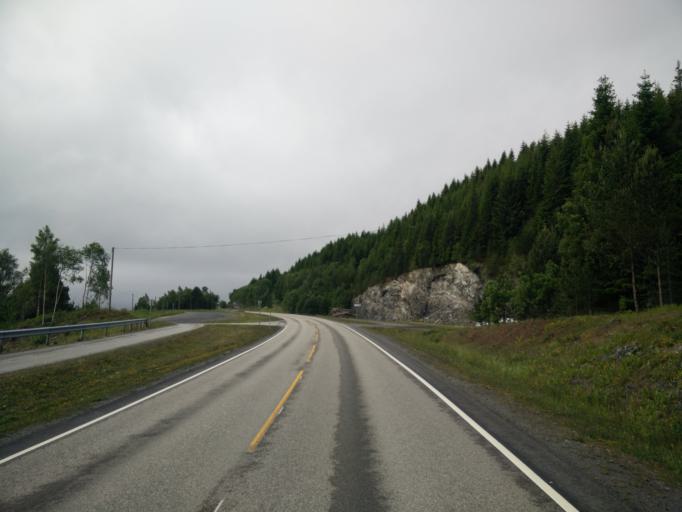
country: NO
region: More og Romsdal
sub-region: Kristiansund
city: Rensvik
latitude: 63.0098
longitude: 7.9655
